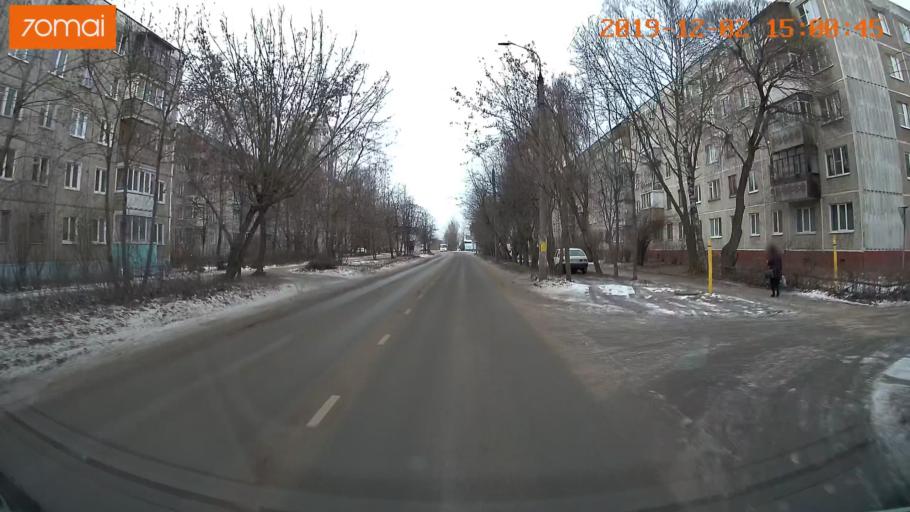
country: RU
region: Ivanovo
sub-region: Gorod Ivanovo
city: Ivanovo
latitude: 56.9720
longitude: 41.0021
